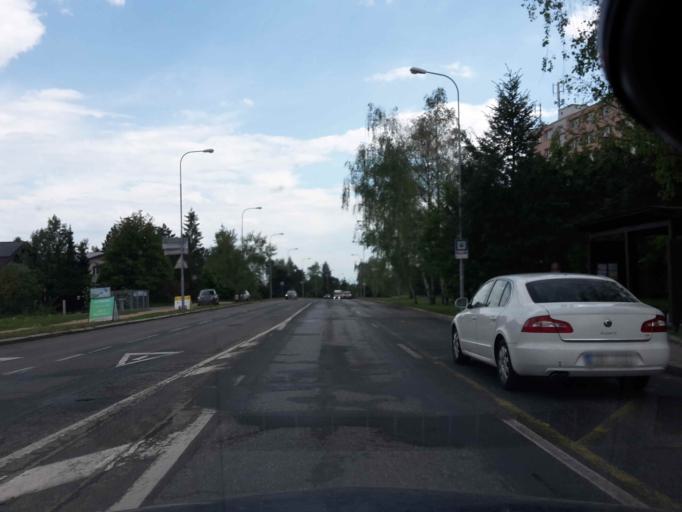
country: CZ
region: South Moravian
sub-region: Mesto Brno
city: Brno
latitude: 49.2337
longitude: 16.6294
